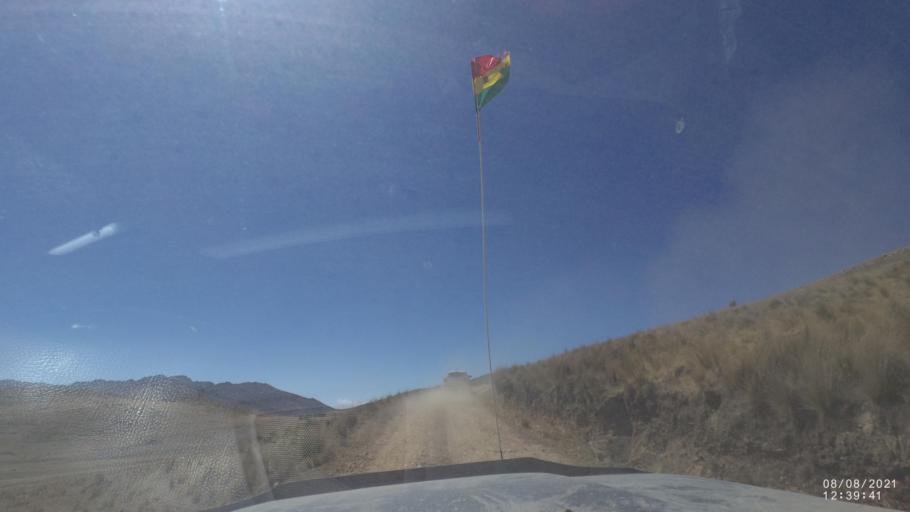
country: BO
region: Cochabamba
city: Colchani
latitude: -16.8271
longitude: -66.6239
